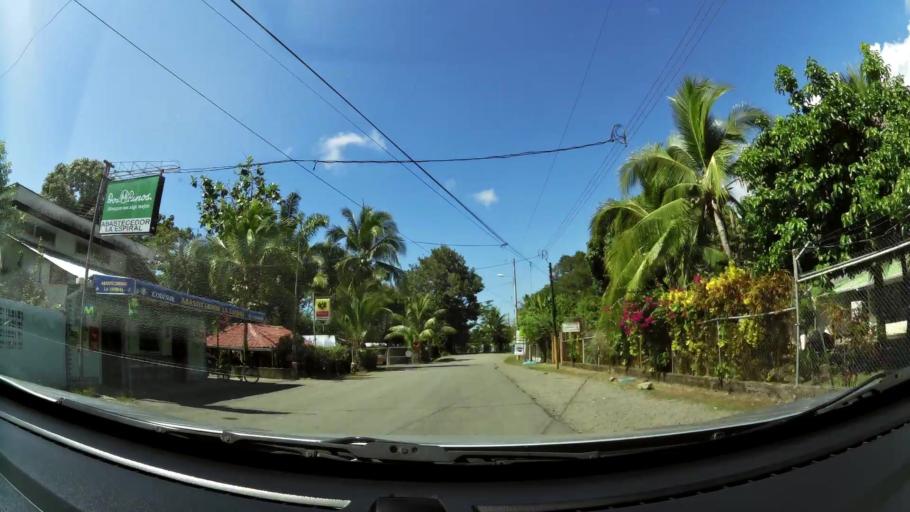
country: CR
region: Puntarenas
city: Quepos
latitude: 9.3305
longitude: -83.9563
